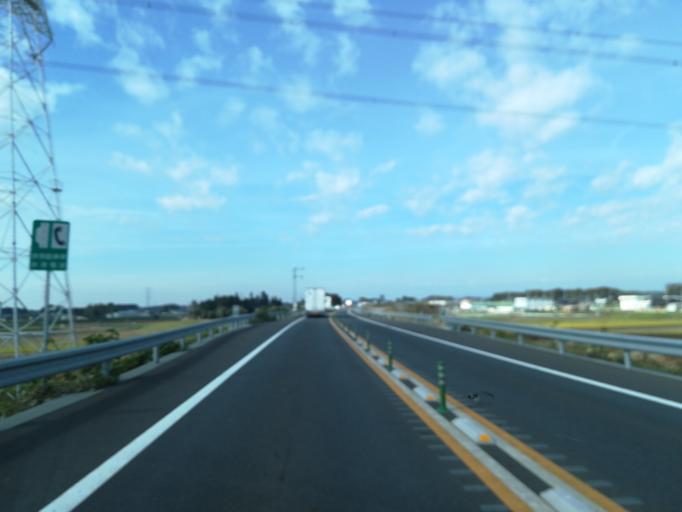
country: JP
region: Ibaraki
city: Sakai
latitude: 36.1154
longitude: 139.8388
